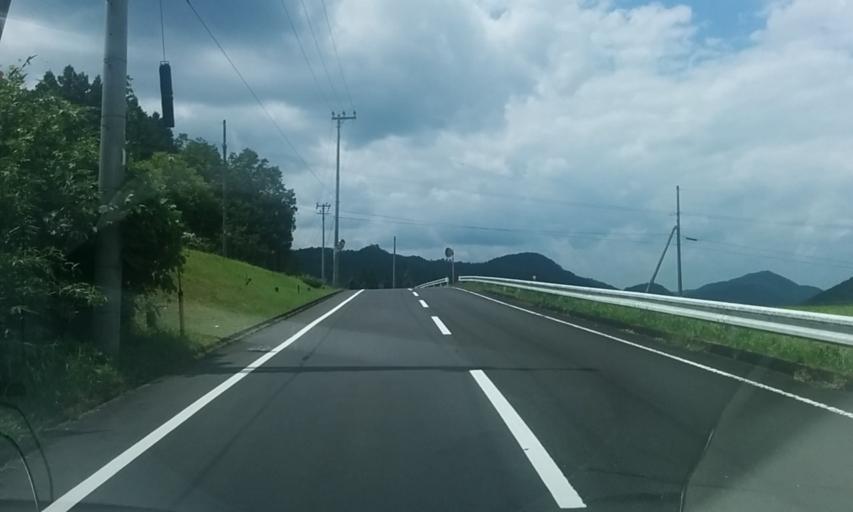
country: JP
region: Kyoto
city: Ayabe
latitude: 35.2872
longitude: 135.2986
